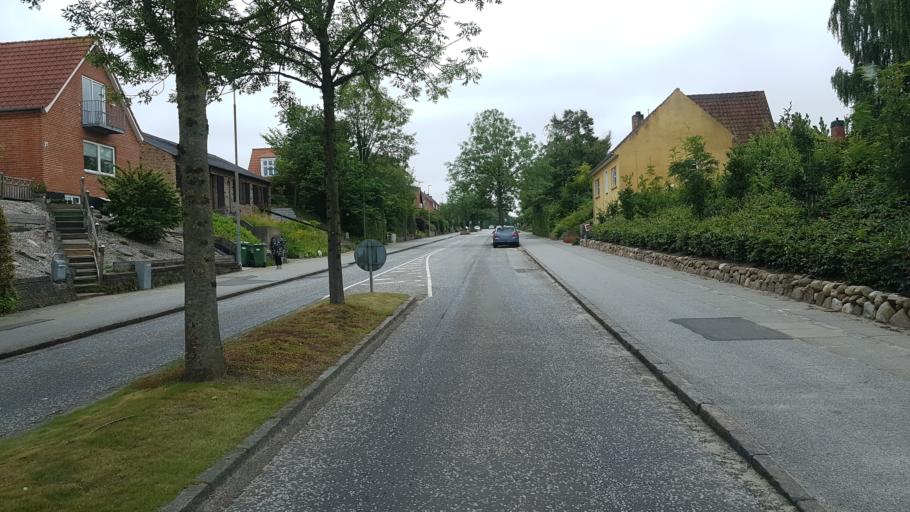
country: DK
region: Central Jutland
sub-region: Struer Kommune
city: Struer
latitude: 56.4892
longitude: 8.5957
